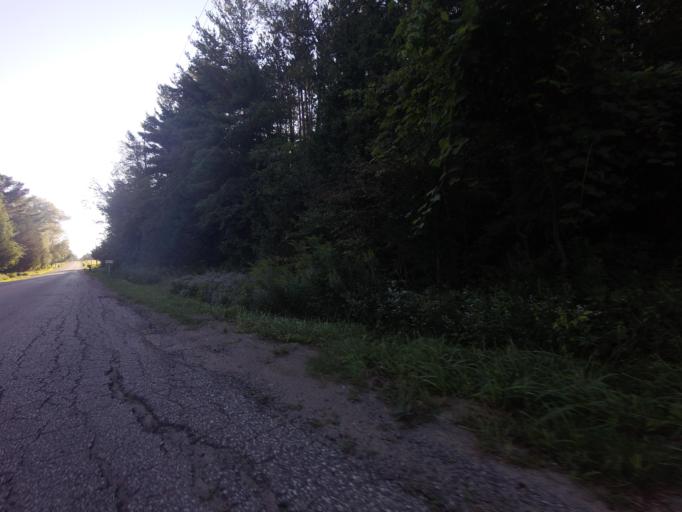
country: CA
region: Ontario
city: Bradford West Gwillimbury
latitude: 44.0470
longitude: -79.7515
